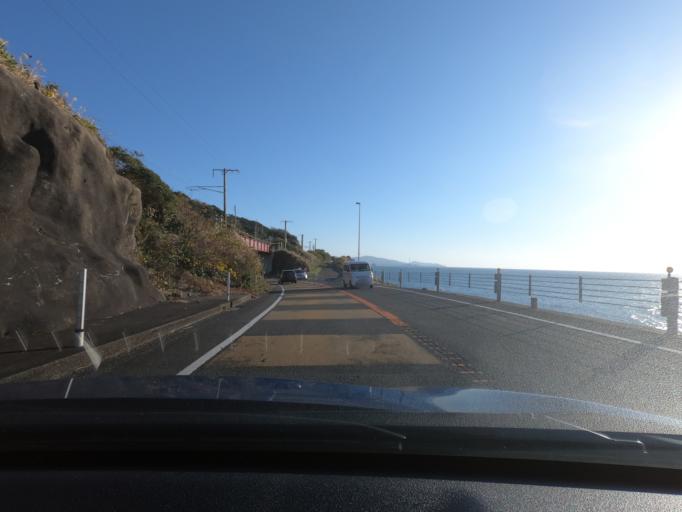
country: JP
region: Kagoshima
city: Akune
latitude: 31.9317
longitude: 130.2202
